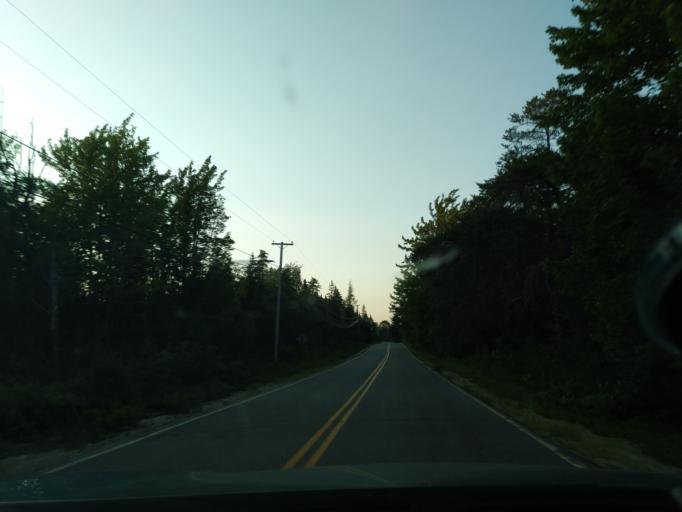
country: US
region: Maine
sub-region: Hancock County
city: Gouldsboro
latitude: 44.3798
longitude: -68.0363
